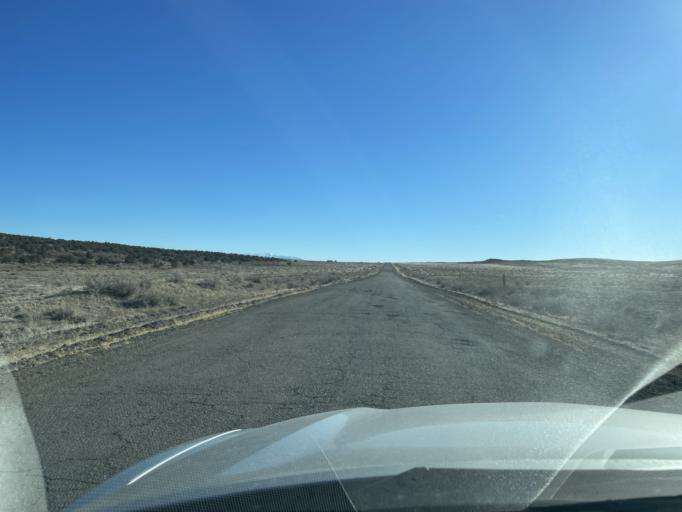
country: US
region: Colorado
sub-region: Mesa County
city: Loma
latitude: 39.1888
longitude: -109.1263
